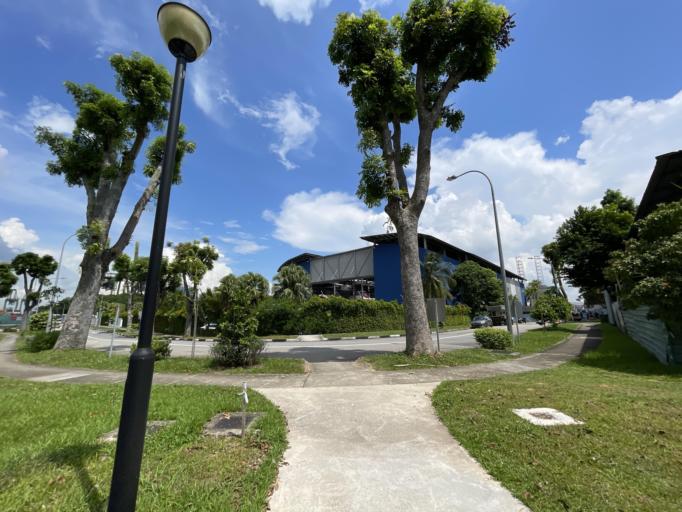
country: SG
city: Singapore
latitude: 1.2934
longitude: 103.7639
